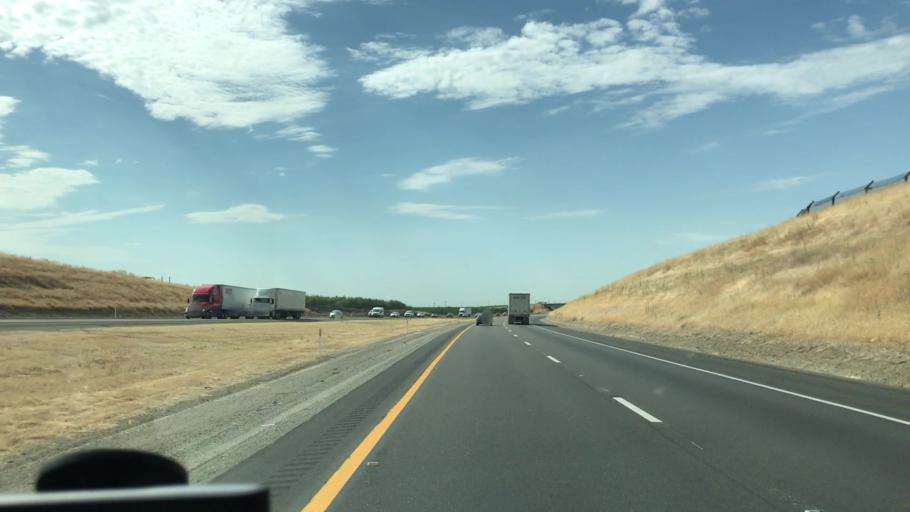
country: US
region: California
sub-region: Stanislaus County
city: Patterson
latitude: 37.3869
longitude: -121.1310
